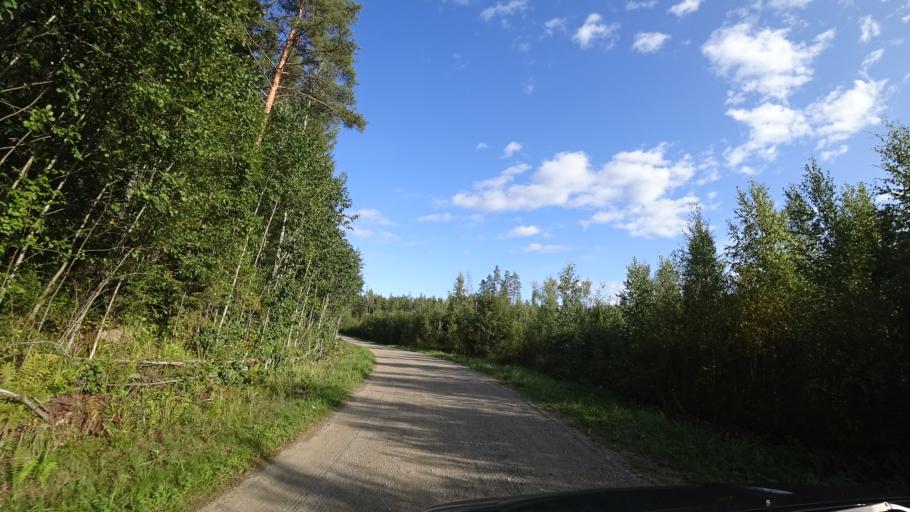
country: FI
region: Paijanne Tavastia
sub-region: Lahti
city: Auttoinen
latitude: 61.2157
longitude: 25.1526
